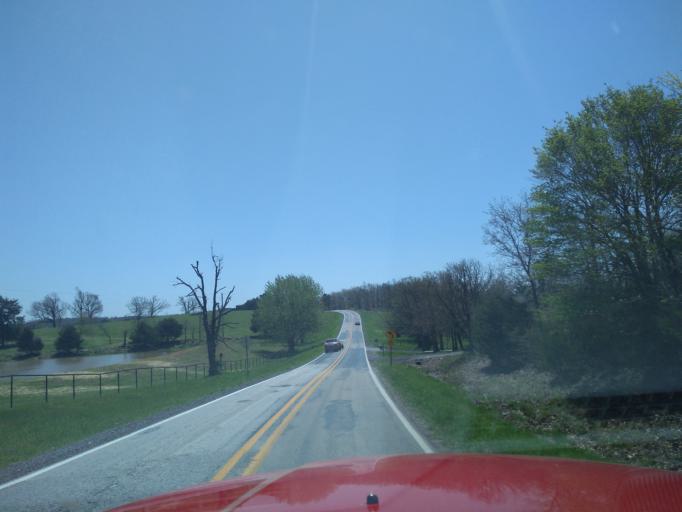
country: US
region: Arkansas
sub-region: Washington County
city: West Fork
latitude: 35.9041
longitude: -94.2202
